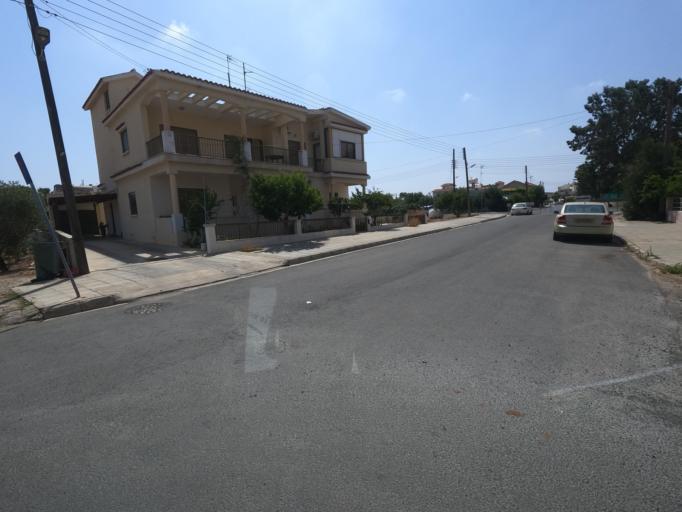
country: CY
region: Ammochostos
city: Deryneia
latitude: 35.0608
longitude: 33.9672
